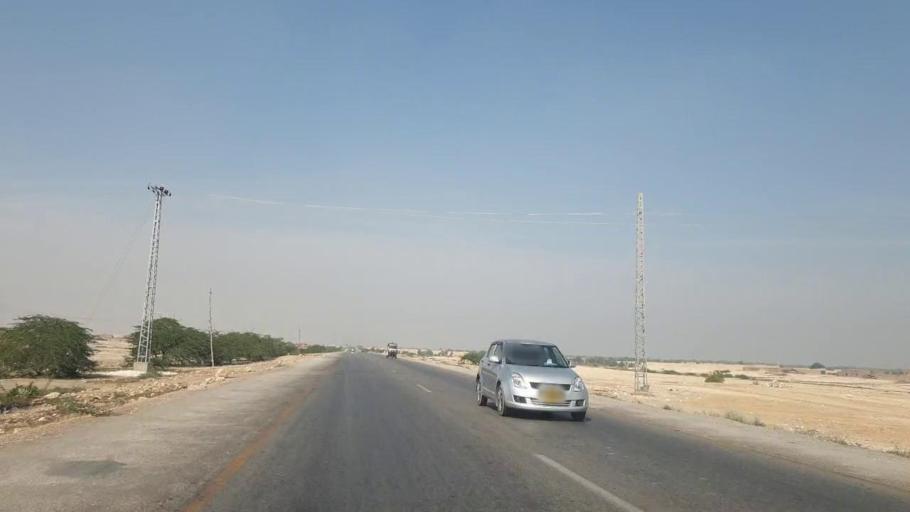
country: PK
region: Sindh
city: Hala
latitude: 25.8051
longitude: 68.2775
